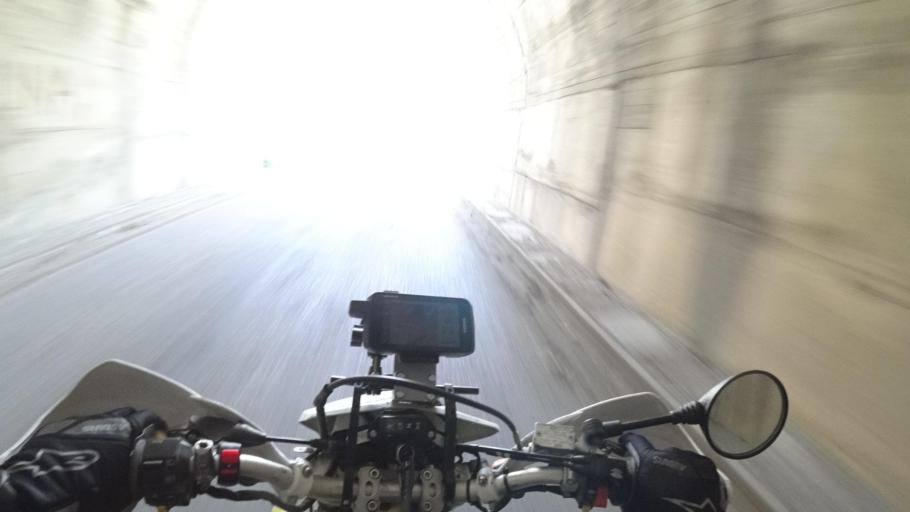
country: BA
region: Federation of Bosnia and Herzegovina
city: Polje-Bijela
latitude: 43.6343
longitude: 17.9890
